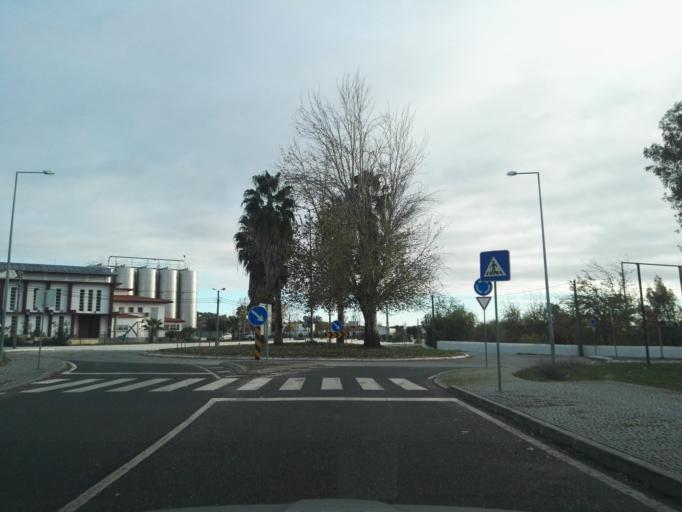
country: PT
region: Evora
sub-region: Redondo
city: Redondo
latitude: 38.6446
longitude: -7.5528
